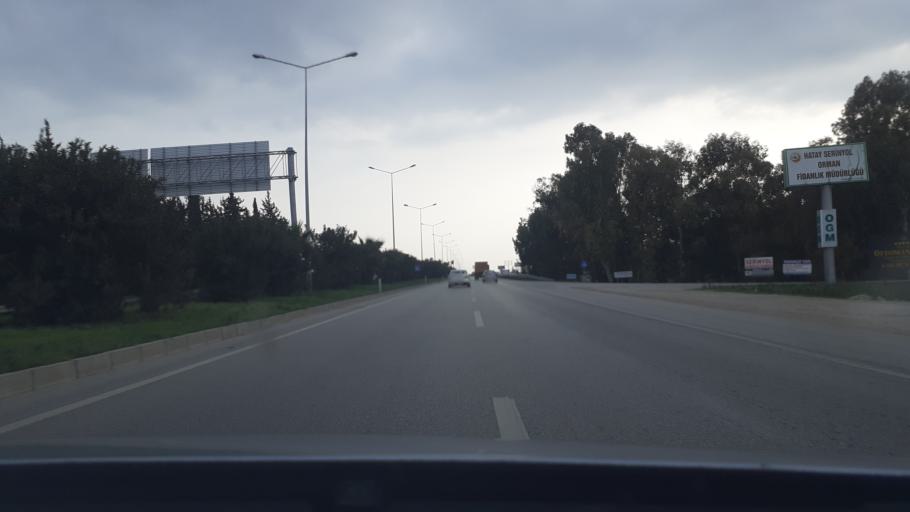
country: TR
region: Hatay
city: Serinyol
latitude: 36.3708
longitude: 36.2252
